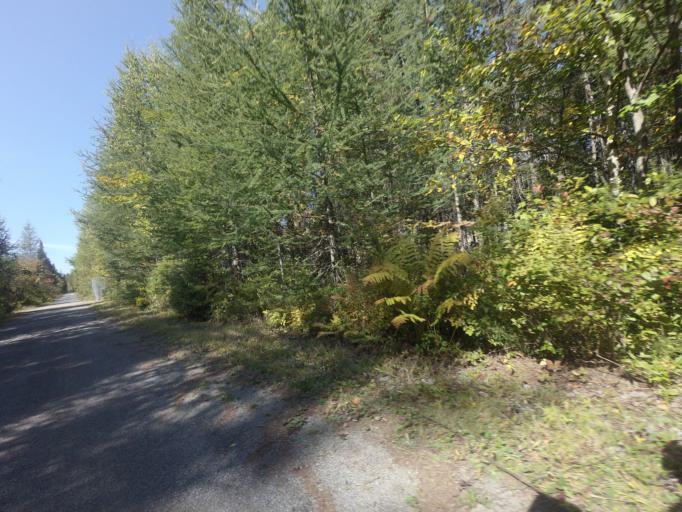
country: CA
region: Quebec
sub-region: Laurentides
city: Sainte-Agathe-des-Monts
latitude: 46.1043
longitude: -74.3837
